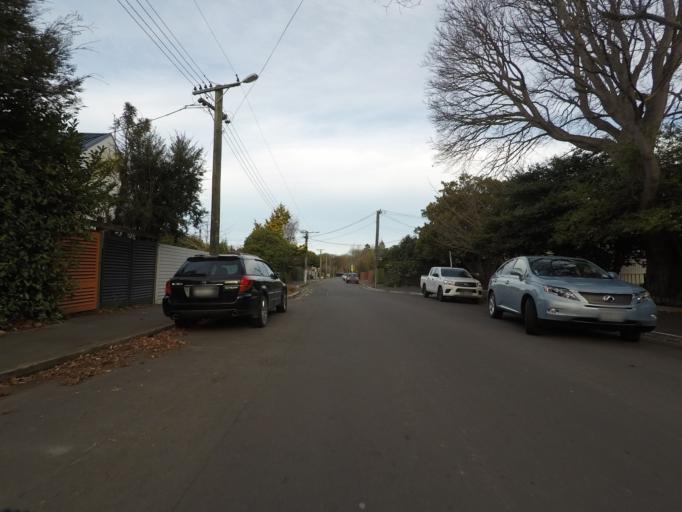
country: NZ
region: Canterbury
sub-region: Christchurch City
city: Christchurch
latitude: -43.5196
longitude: 172.6187
